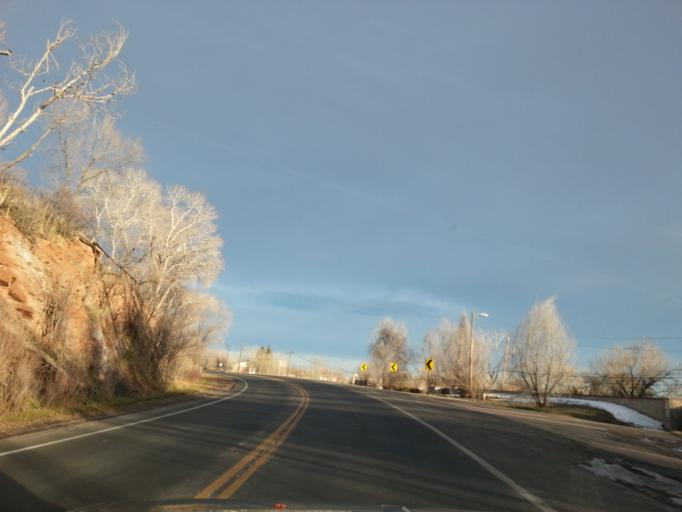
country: US
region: Colorado
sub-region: Larimer County
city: Loveland
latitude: 40.4067
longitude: -105.1435
